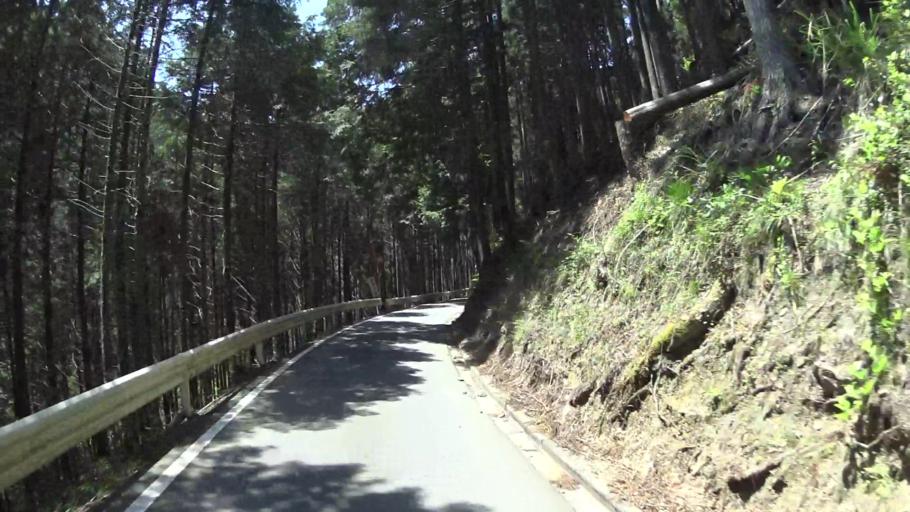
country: JP
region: Kyoto
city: Kameoka
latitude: 35.1307
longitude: 135.5829
